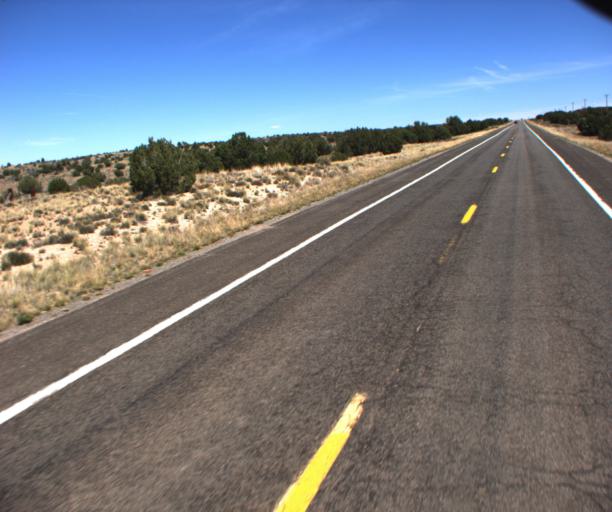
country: US
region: Arizona
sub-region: Mohave County
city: Peach Springs
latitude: 35.4969
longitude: -113.5384
